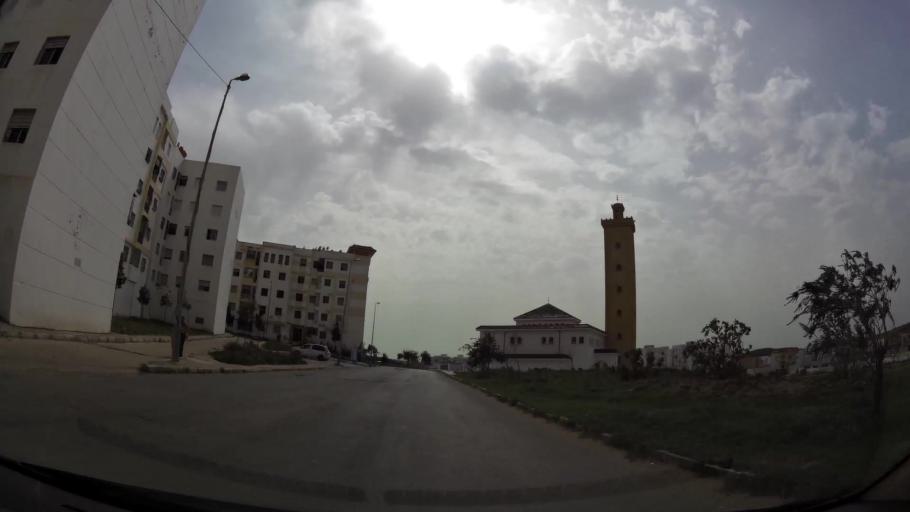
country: MA
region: Tanger-Tetouan
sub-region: Tanger-Assilah
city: Boukhalef
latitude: 35.7433
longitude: -5.8858
